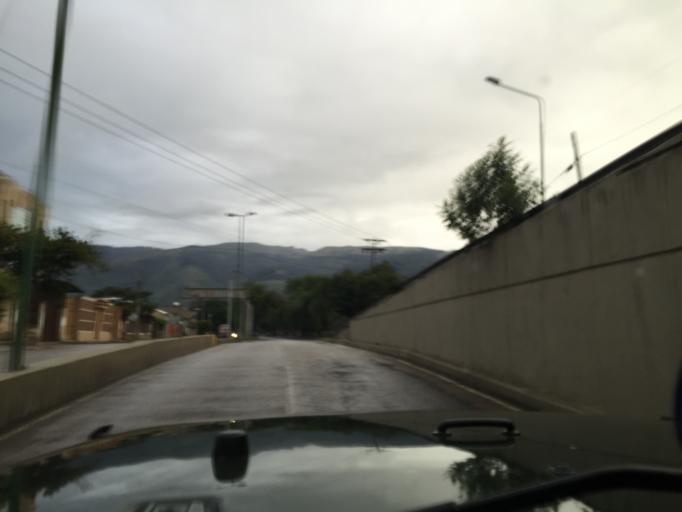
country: BO
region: Cochabamba
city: Cochabamba
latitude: -17.3938
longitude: -66.1675
